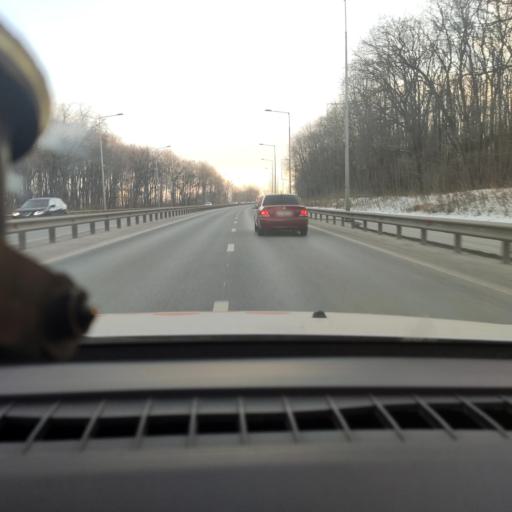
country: RU
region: Samara
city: Petra-Dubrava
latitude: 53.2850
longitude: 50.2507
